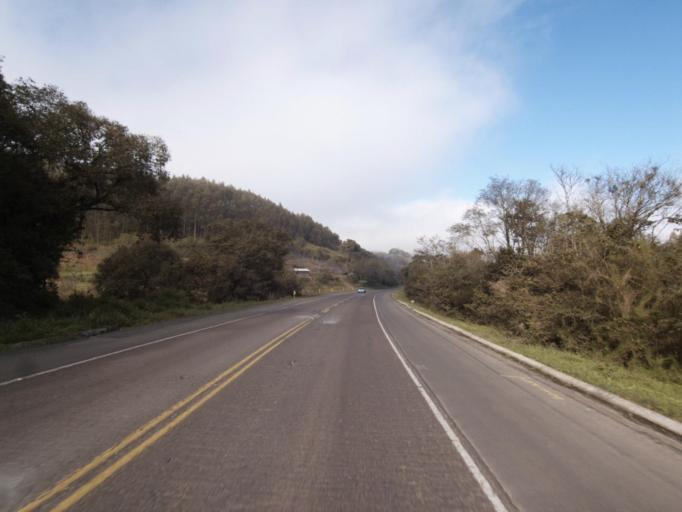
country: BR
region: Rio Grande do Sul
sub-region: Frederico Westphalen
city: Frederico Westphalen
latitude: -27.0114
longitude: -53.2251
